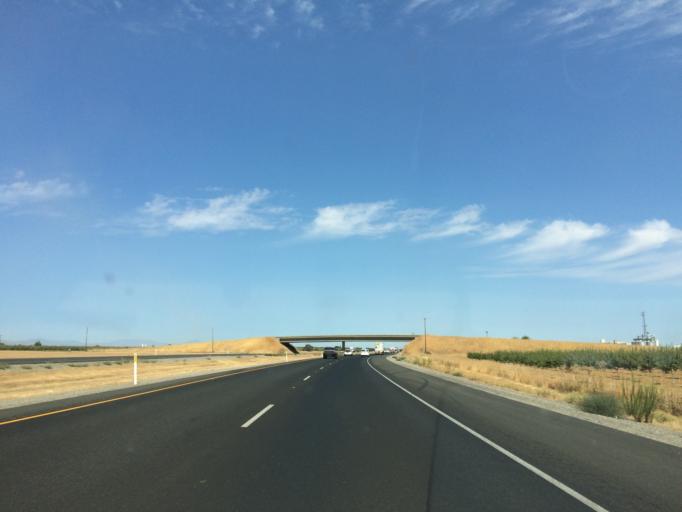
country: US
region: California
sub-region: Colusa County
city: Arbuckle
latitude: 38.9530
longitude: -122.0170
